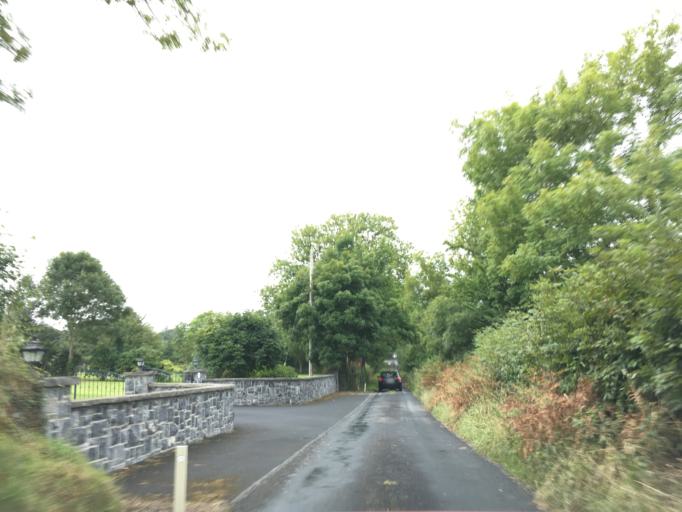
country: IE
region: Munster
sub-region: An Clar
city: Ennis
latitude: 52.7288
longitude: -9.0839
